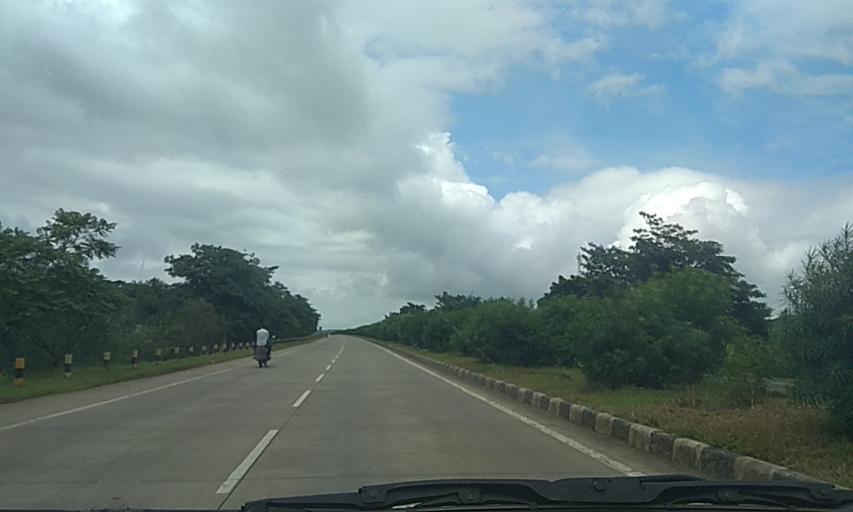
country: IN
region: Karnataka
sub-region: Belgaum
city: Sankeshwar
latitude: 16.3081
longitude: 74.4310
